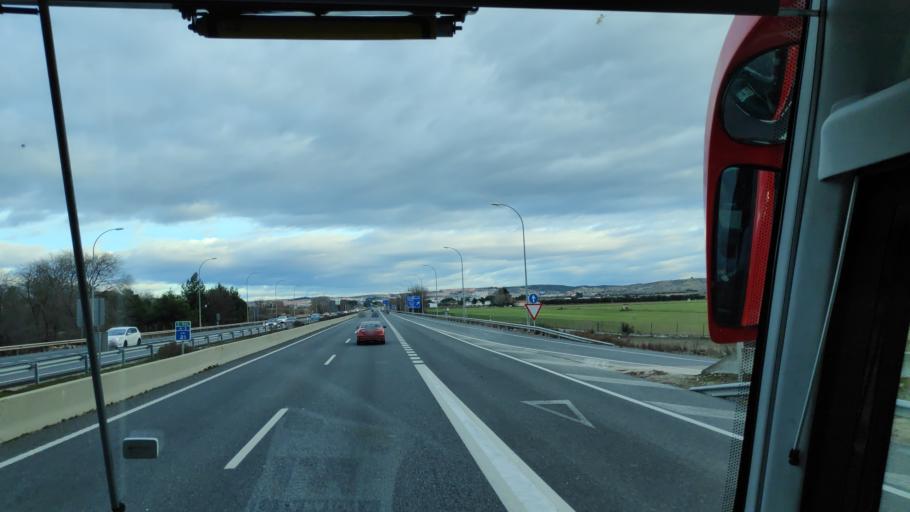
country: ES
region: Madrid
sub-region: Provincia de Madrid
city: Vaciamadrid
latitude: 40.3165
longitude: -3.5082
